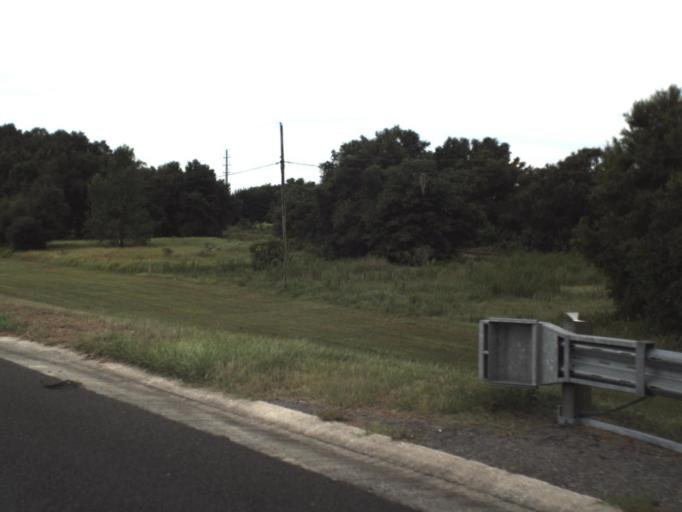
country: US
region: Florida
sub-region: Polk County
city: Fort Meade
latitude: 27.8145
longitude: -81.8210
